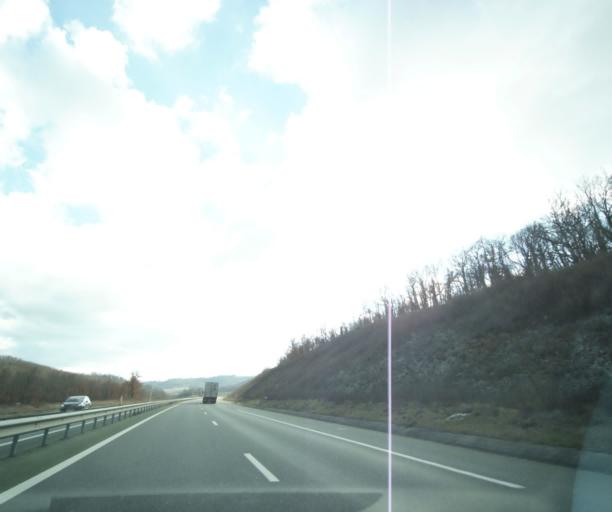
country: FR
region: Midi-Pyrenees
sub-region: Departement du Lot
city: Le Vigan
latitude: 44.7662
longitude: 1.5398
